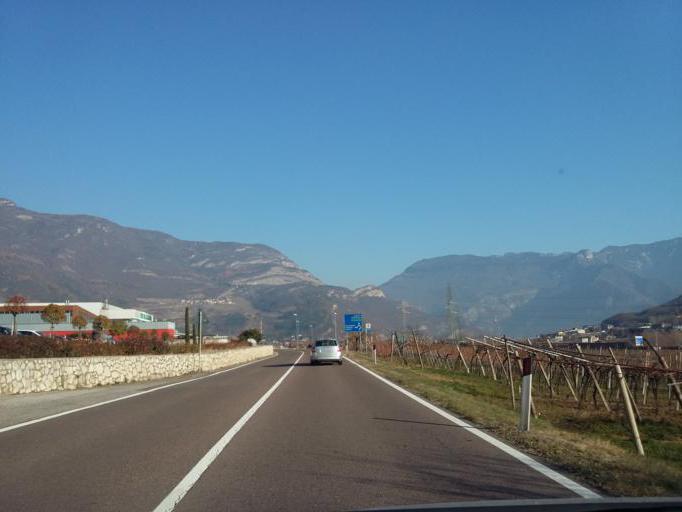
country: IT
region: Trentino-Alto Adige
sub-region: Provincia di Trento
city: Nogaredo
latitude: 45.9088
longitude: 11.0285
